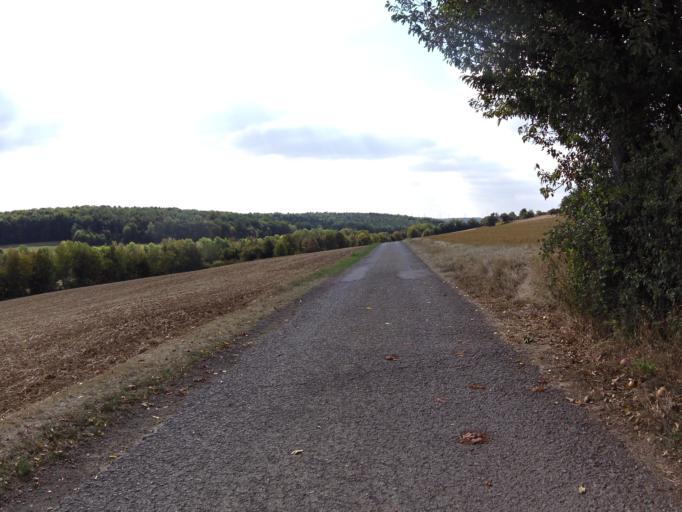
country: DE
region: Bavaria
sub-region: Regierungsbezirk Unterfranken
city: Hettstadt
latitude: 49.7836
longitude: 9.8146
